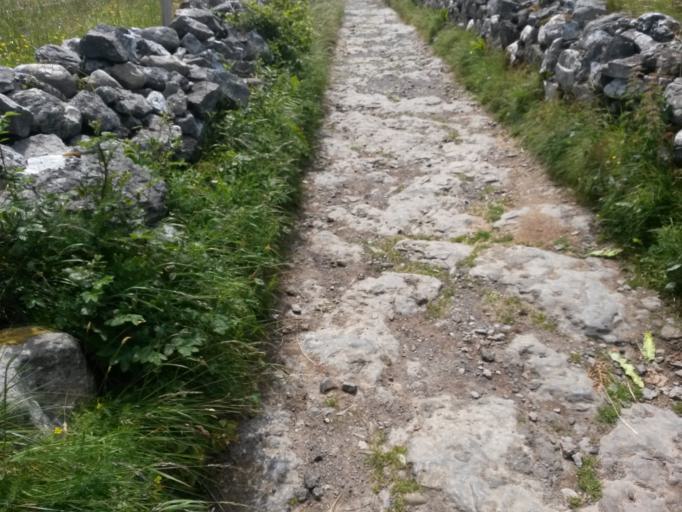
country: IE
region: Connaught
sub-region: Sligo
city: Strandhill
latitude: 54.2539
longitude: -8.5594
